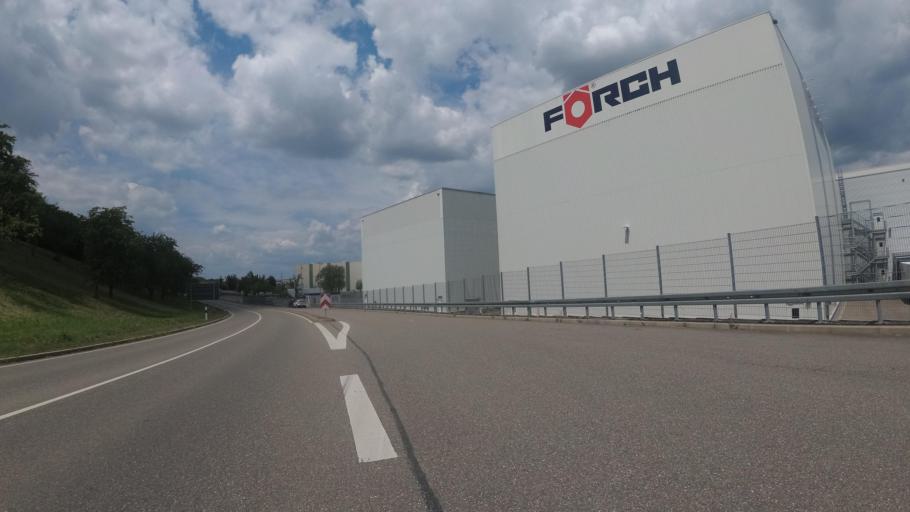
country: DE
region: Baden-Wuerttemberg
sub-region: Regierungsbezirk Stuttgart
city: Neuenstadt am Kocher
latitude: 49.2396
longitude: 9.3082
